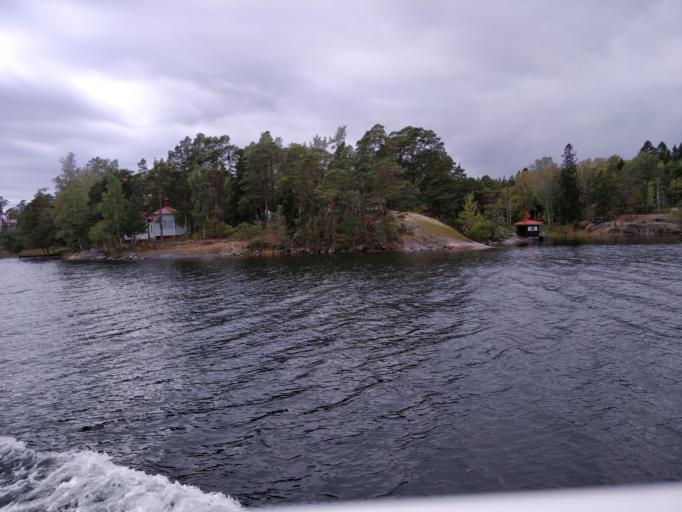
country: FI
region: Uusimaa
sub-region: Helsinki
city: Vantaa
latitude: 60.1617
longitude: 25.0995
